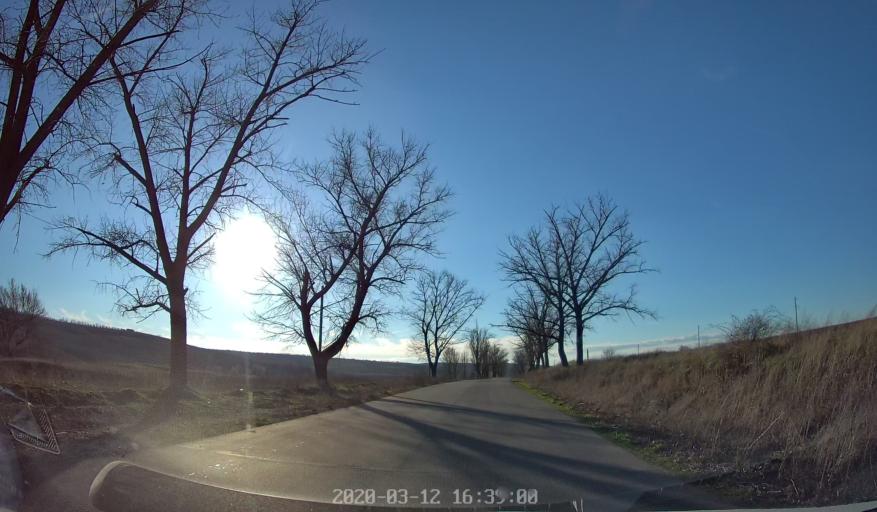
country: MD
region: Anenii Noi
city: Anenii Noi
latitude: 46.8142
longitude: 29.1729
